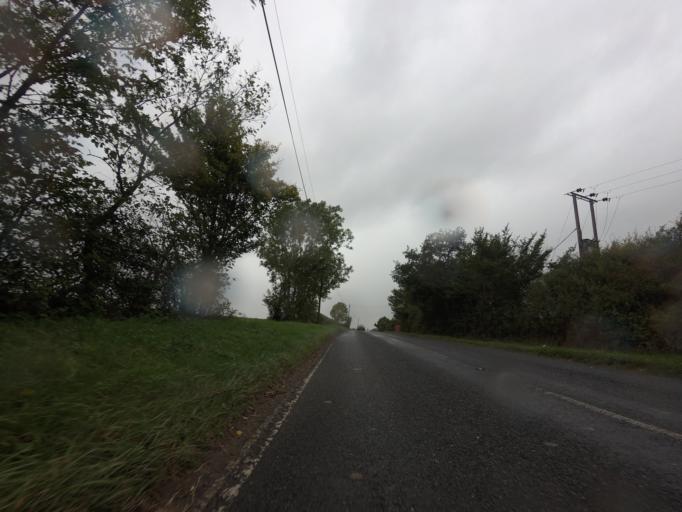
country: GB
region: England
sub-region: Cambridgeshire
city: Wimpole
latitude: 52.1841
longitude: -0.0555
